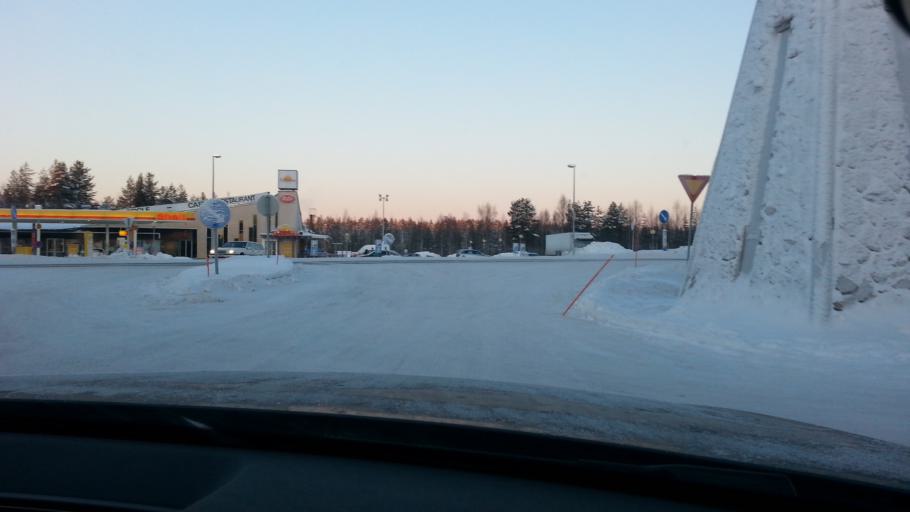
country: FI
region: Lapland
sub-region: Rovaniemi
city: Rovaniemi
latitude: 66.5438
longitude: 25.8446
